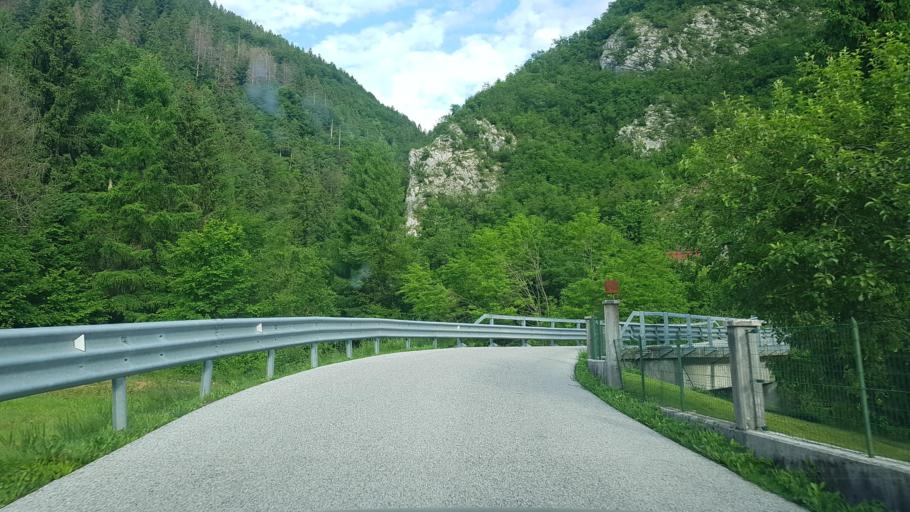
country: IT
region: Friuli Venezia Giulia
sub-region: Provincia di Udine
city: Zuglio
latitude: 46.4640
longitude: 13.0208
